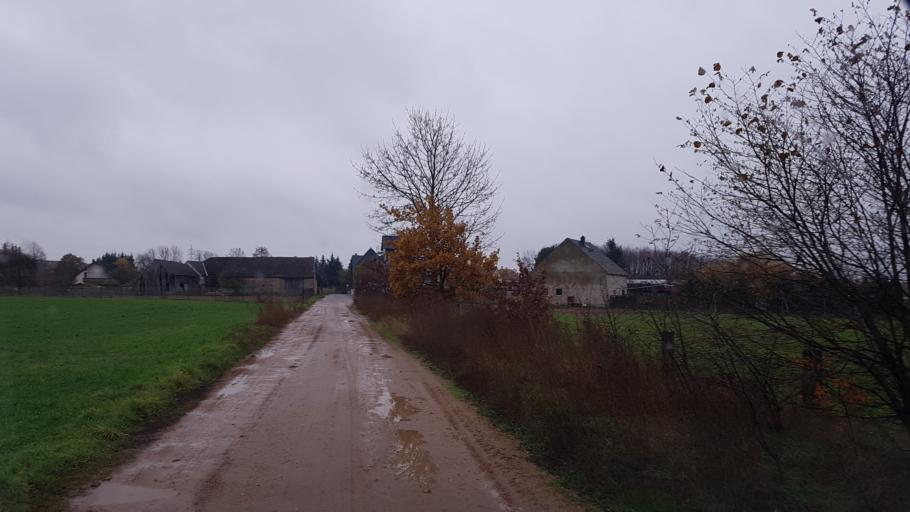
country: DE
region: Brandenburg
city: Herzberg
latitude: 51.6619
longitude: 13.2212
